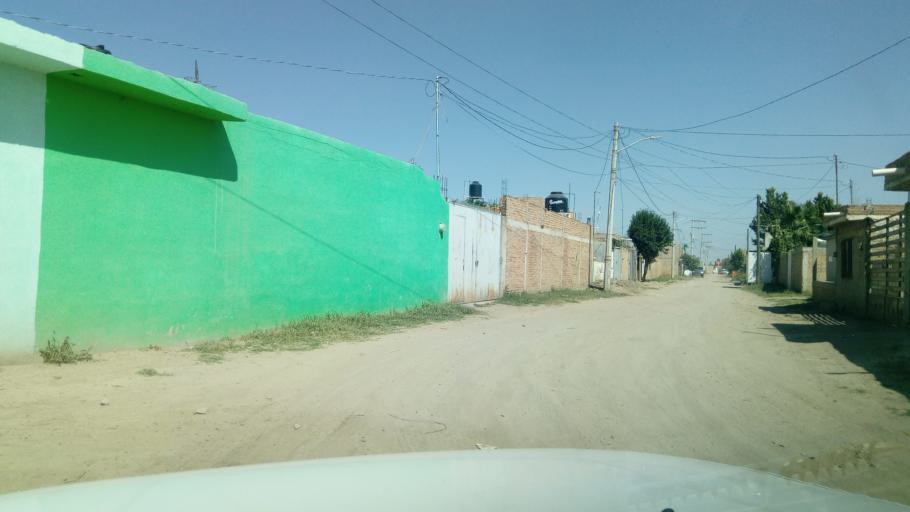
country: MX
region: Durango
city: Victoria de Durango
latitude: 23.9959
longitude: -104.6949
